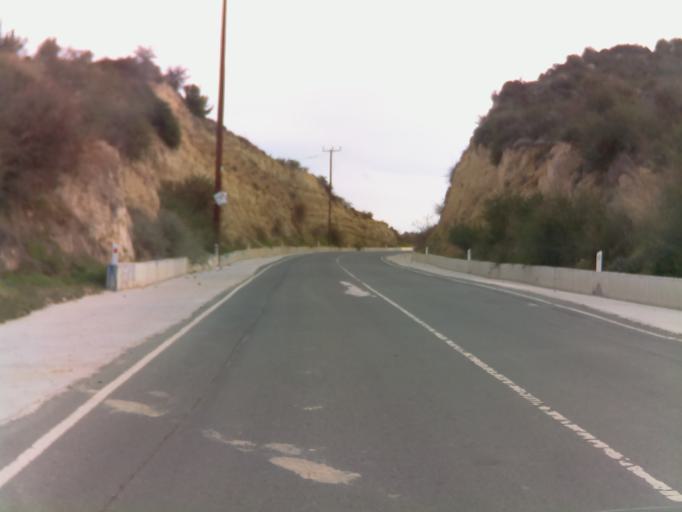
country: CY
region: Pafos
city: Polis
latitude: 35.0036
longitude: 32.4042
